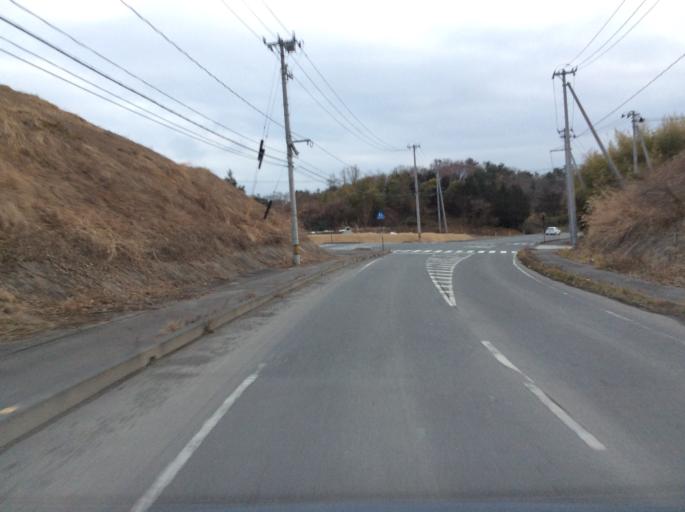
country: JP
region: Fukushima
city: Iwaki
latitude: 37.1206
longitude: 140.9793
